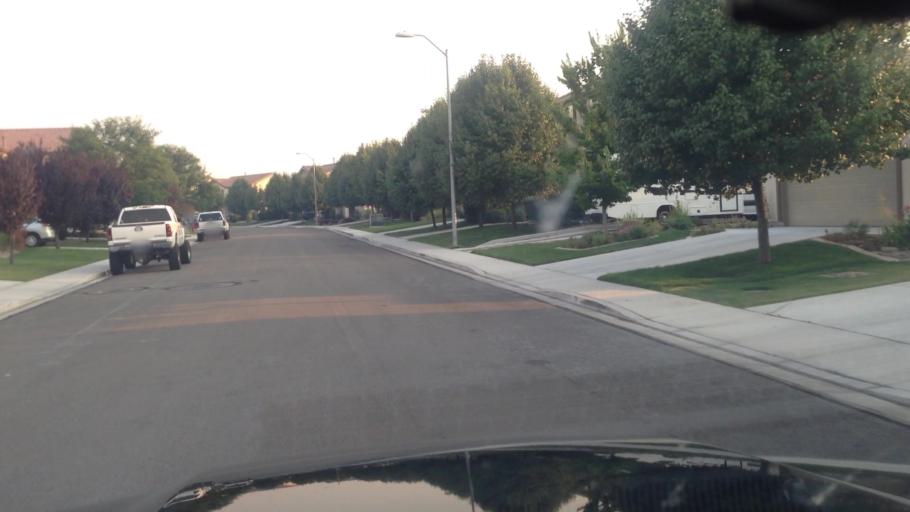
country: US
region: Nevada
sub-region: Washoe County
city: Sparks
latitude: 39.4100
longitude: -119.7404
